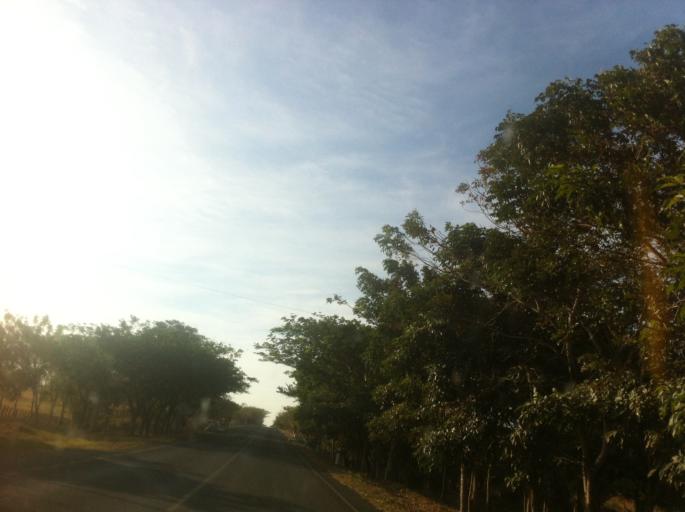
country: NI
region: Rivas
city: Rivas
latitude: 11.3324
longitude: -85.7238
